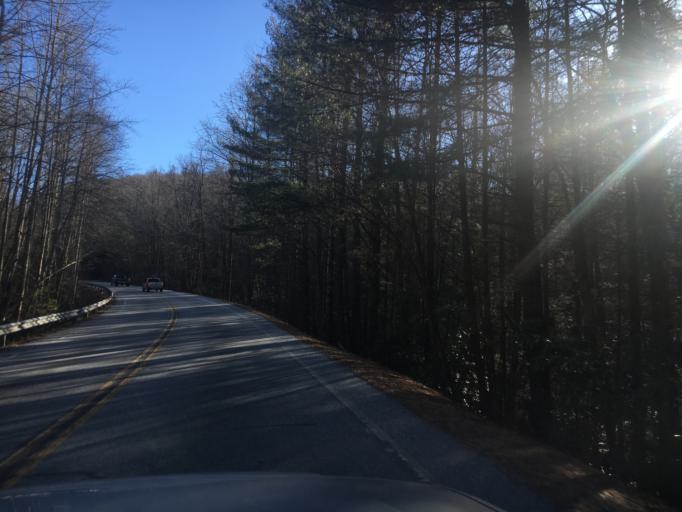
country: US
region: Georgia
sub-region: Union County
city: Blairsville
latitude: 34.7428
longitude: -83.9210
